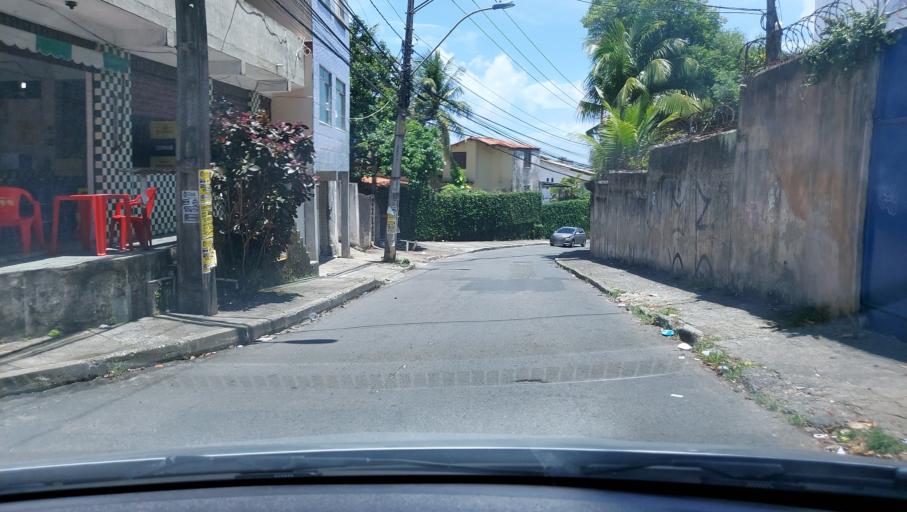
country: BR
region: Bahia
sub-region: Salvador
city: Salvador
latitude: -12.9868
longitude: -38.4730
